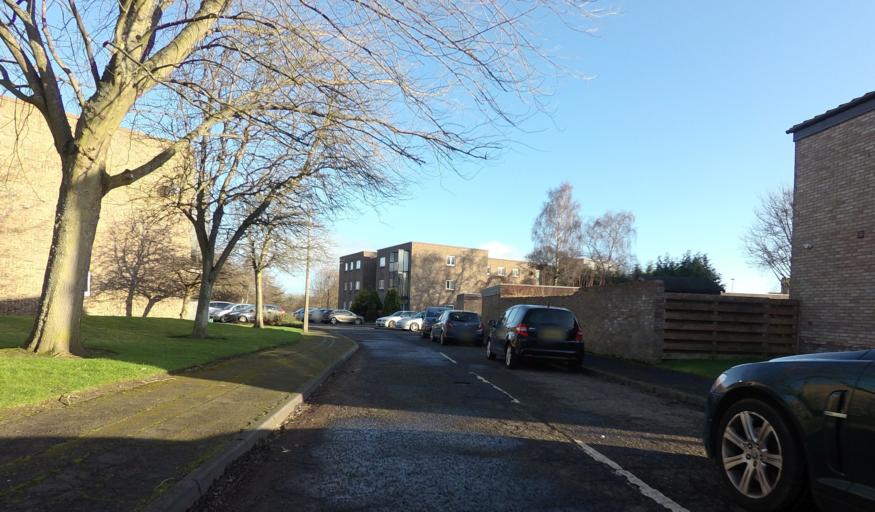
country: GB
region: Scotland
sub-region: Edinburgh
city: Currie
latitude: 55.9723
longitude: -3.3092
